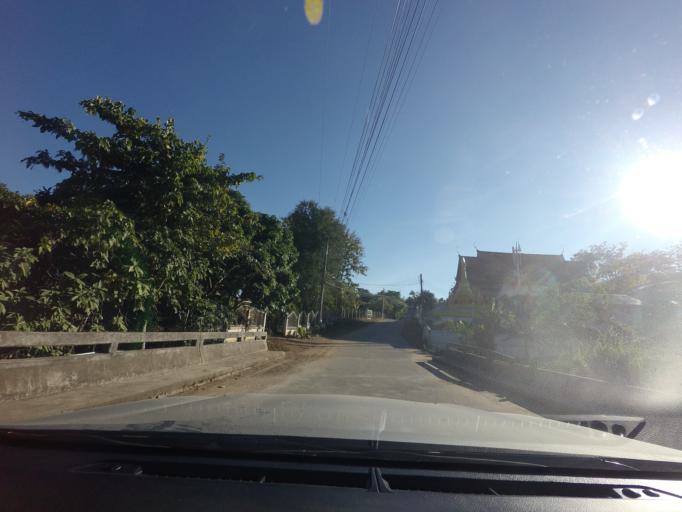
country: TH
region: Mae Hong Son
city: Wiang Nuea
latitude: 19.3953
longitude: 98.4218
